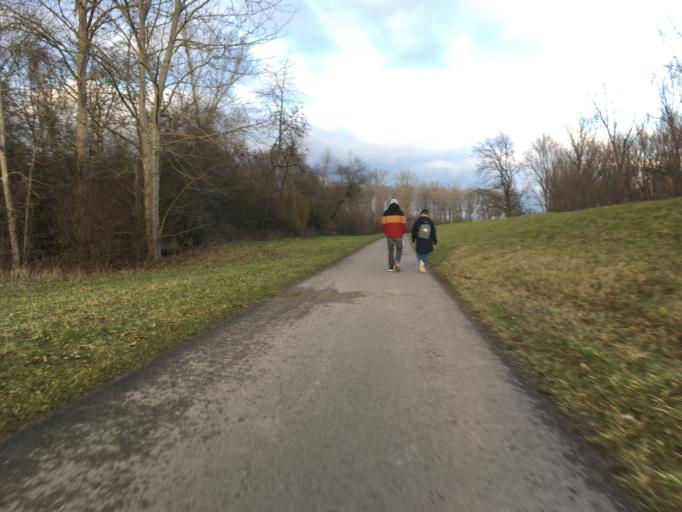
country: DE
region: Rheinland-Pfalz
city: Speyer
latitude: 49.2927
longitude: 8.4234
